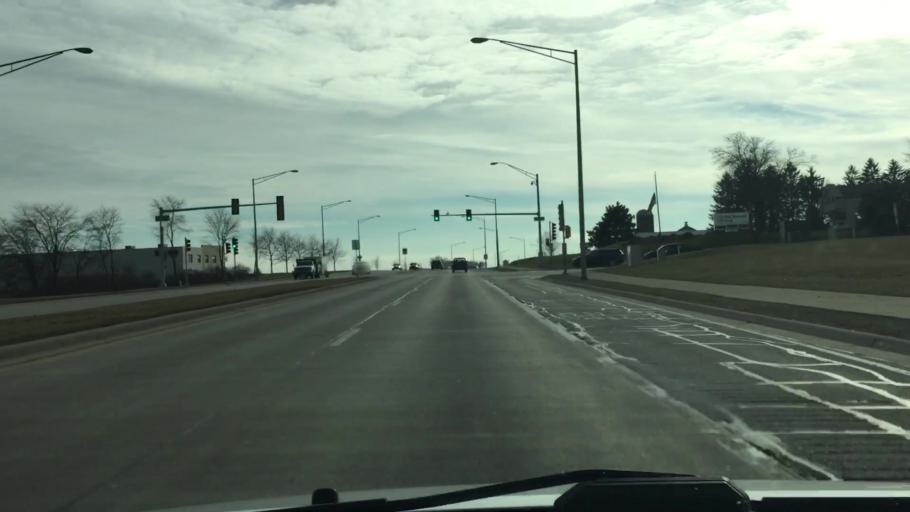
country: US
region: Illinois
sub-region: Kane County
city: Saint Charles
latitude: 41.9084
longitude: -88.2775
